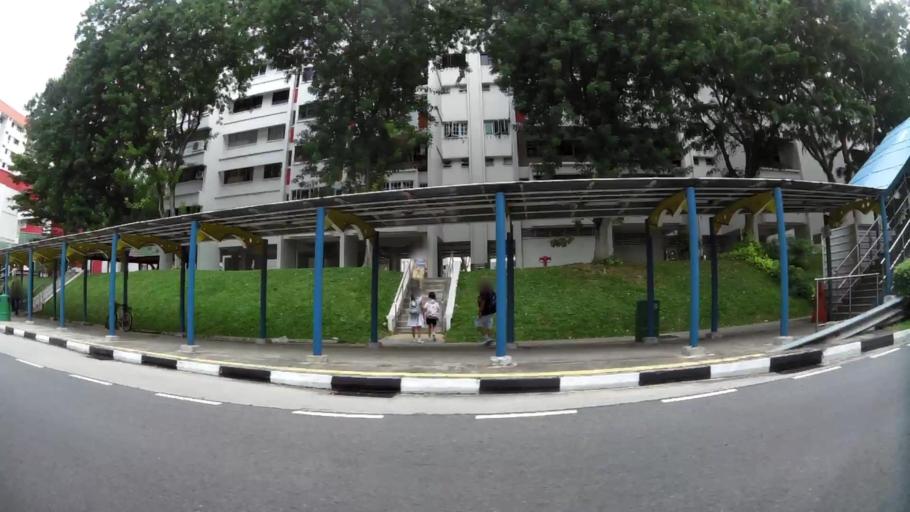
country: SG
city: Singapore
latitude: 1.3534
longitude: 103.9463
